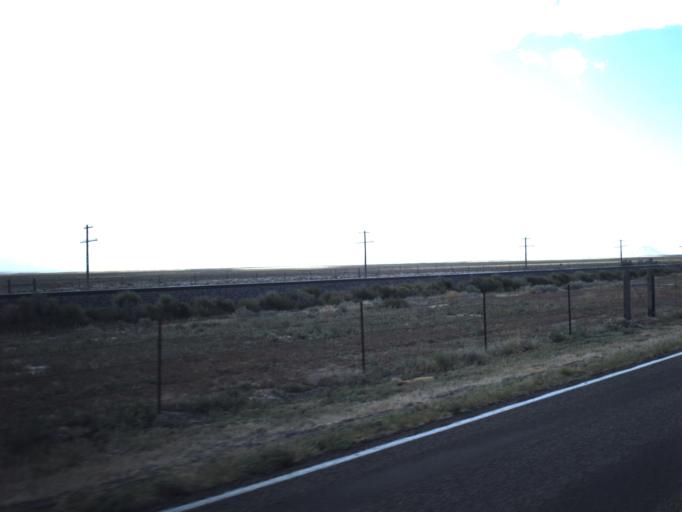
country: US
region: Utah
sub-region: Millard County
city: Delta
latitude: 39.0202
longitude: -112.7795
